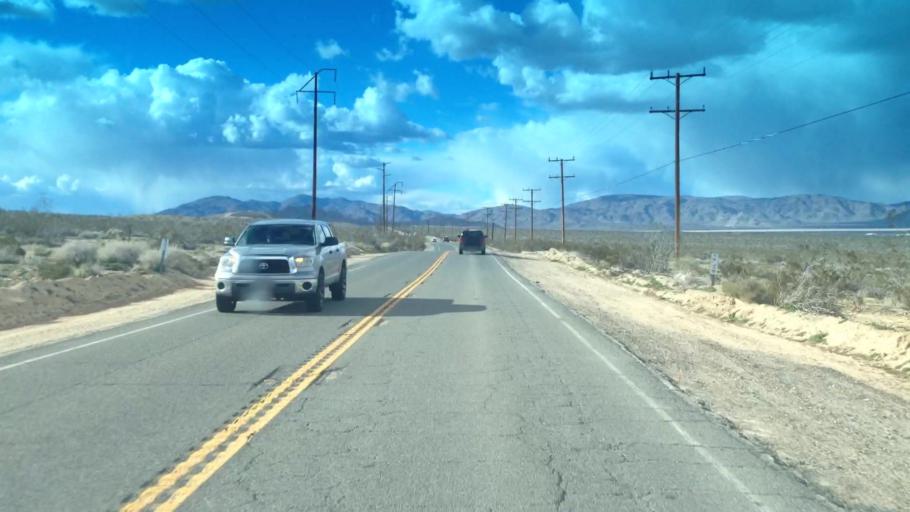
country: US
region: California
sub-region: San Bernardino County
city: Lucerne Valley
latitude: 34.4181
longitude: -116.9123
